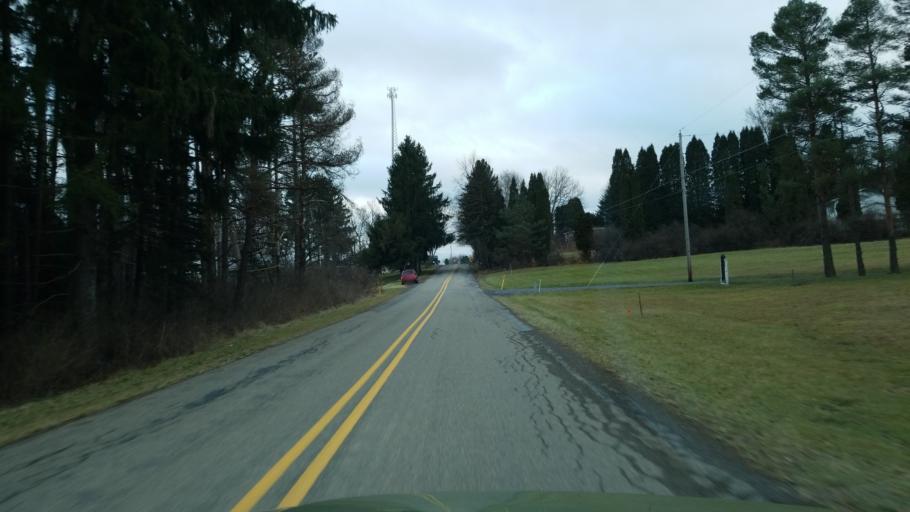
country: US
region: Pennsylvania
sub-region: Jefferson County
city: Falls Creek
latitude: 41.1690
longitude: -78.8117
